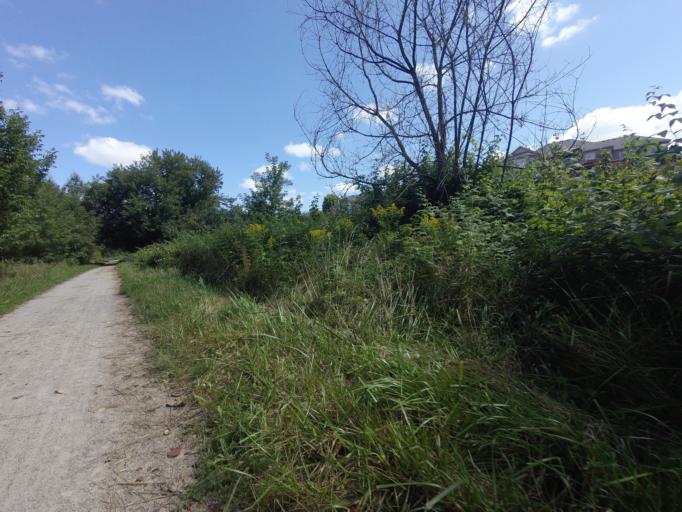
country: CA
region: Ontario
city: Orangeville
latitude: 43.7918
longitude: -80.3134
